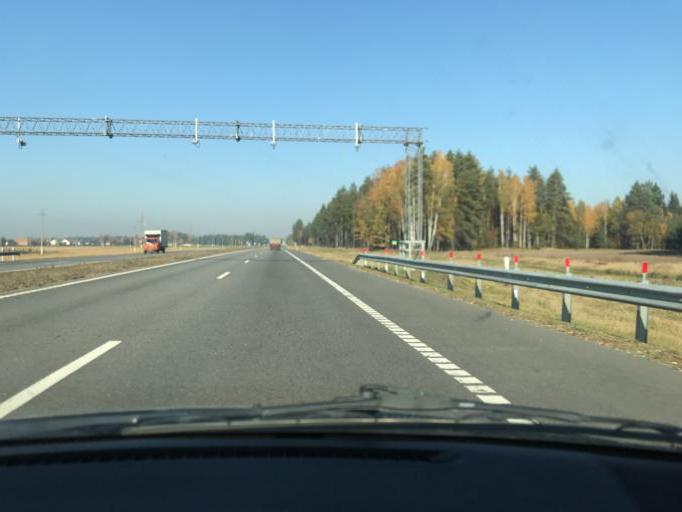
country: BY
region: Minsk
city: Slutsk
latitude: 53.3181
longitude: 27.5359
